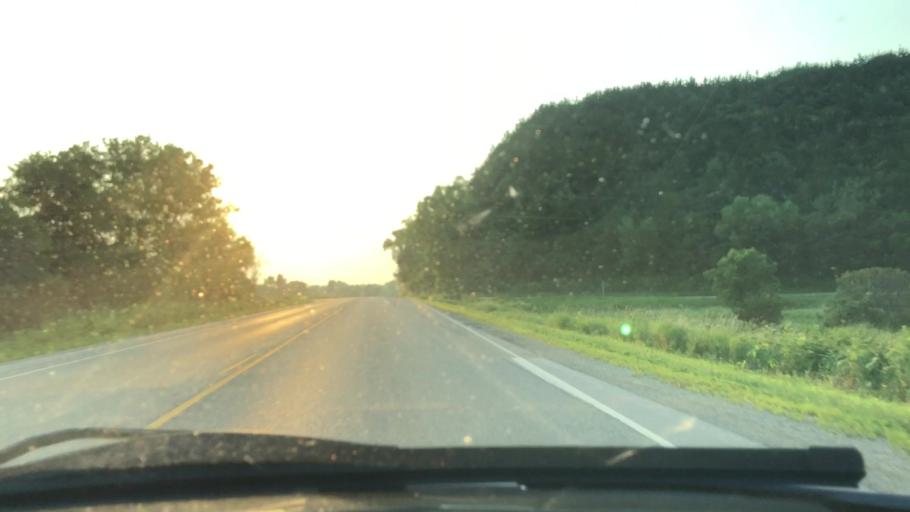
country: US
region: Wisconsin
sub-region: Dane County
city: Black Earth
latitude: 43.1344
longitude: -89.7310
